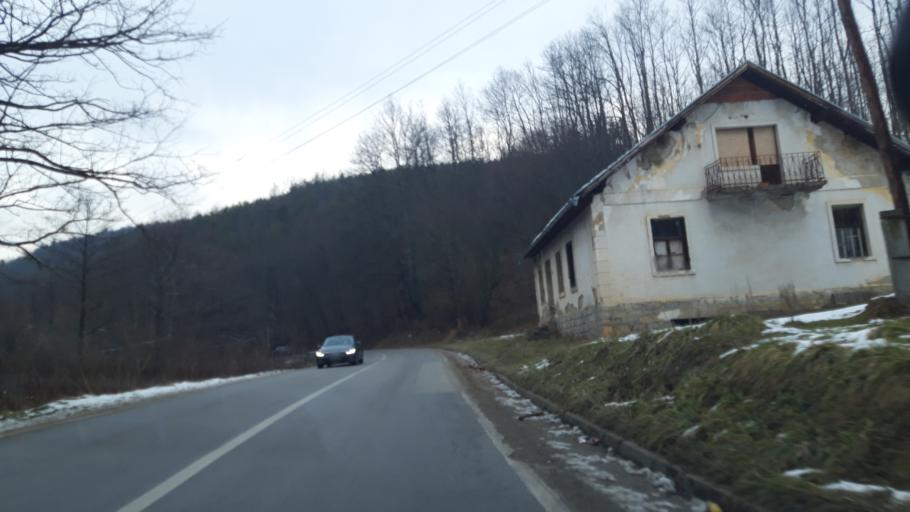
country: BA
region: Republika Srpska
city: Milici
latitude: 44.1677
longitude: 19.0331
